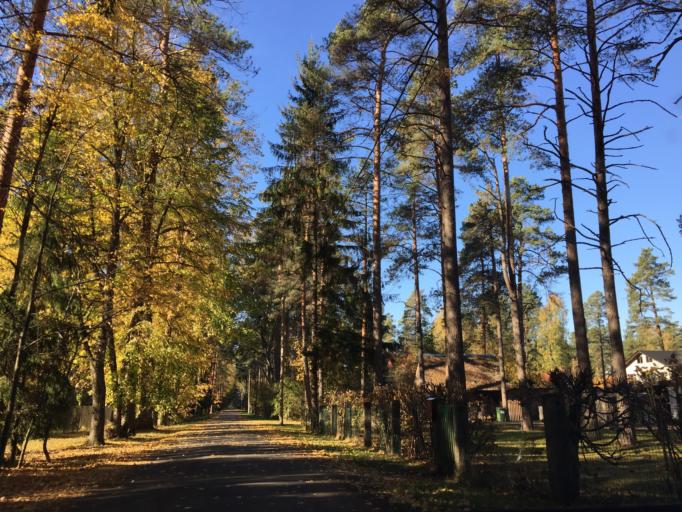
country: LV
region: Incukalns
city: Incukalns
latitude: 57.1005
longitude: 24.6768
